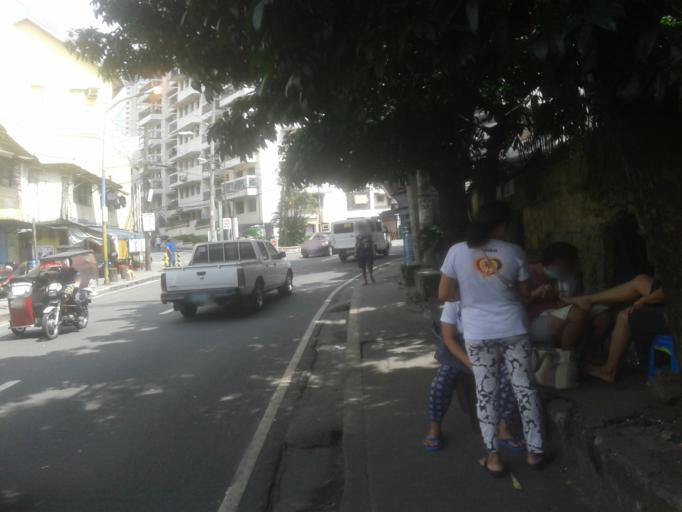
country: PH
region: Metro Manila
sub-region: Mandaluyong
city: Mandaluyong City
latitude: 14.5867
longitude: 121.0428
